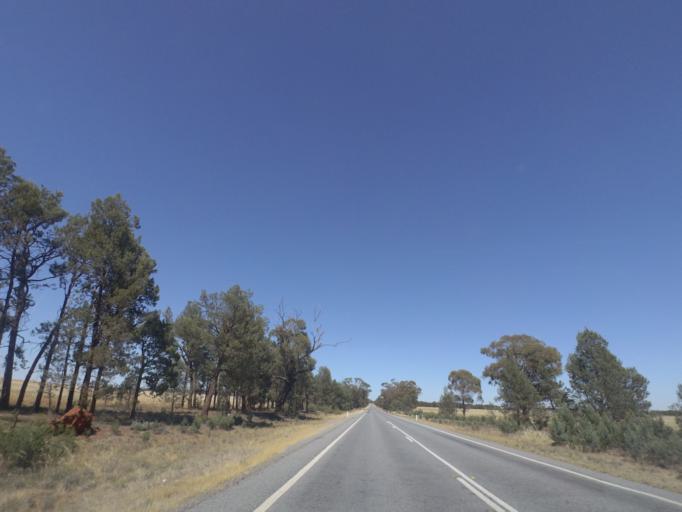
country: AU
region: New South Wales
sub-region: Narrandera
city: Narrandera
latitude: -34.4149
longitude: 146.8630
